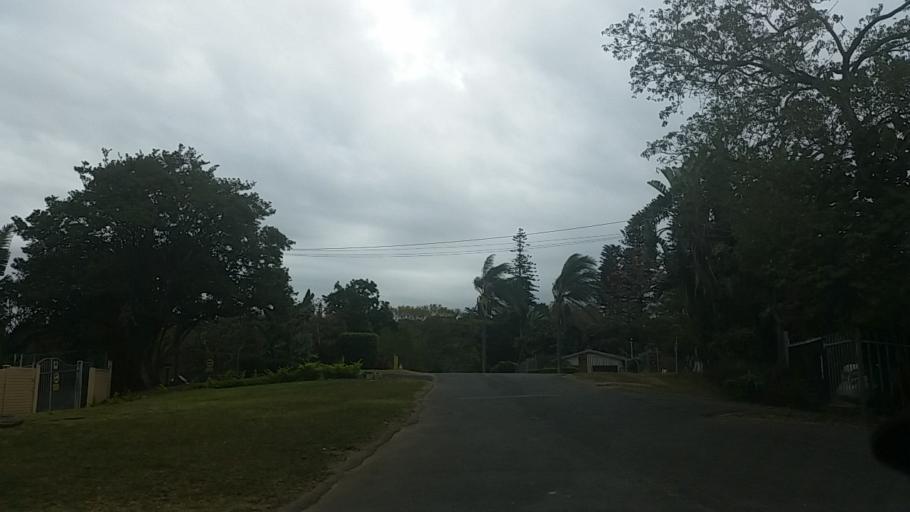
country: ZA
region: KwaZulu-Natal
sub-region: eThekwini Metropolitan Municipality
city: Berea
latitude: -29.8421
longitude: 30.9430
